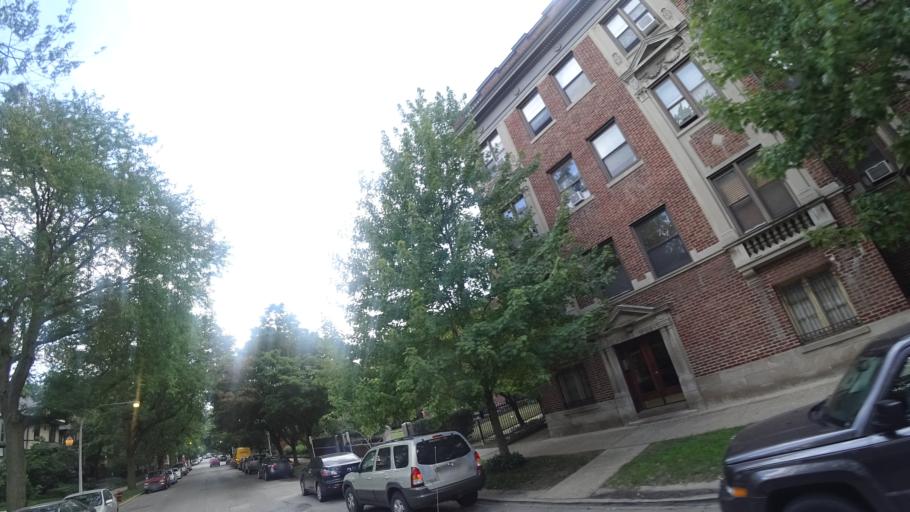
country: US
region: Illinois
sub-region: Cook County
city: Chicago
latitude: 41.8020
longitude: -87.5967
